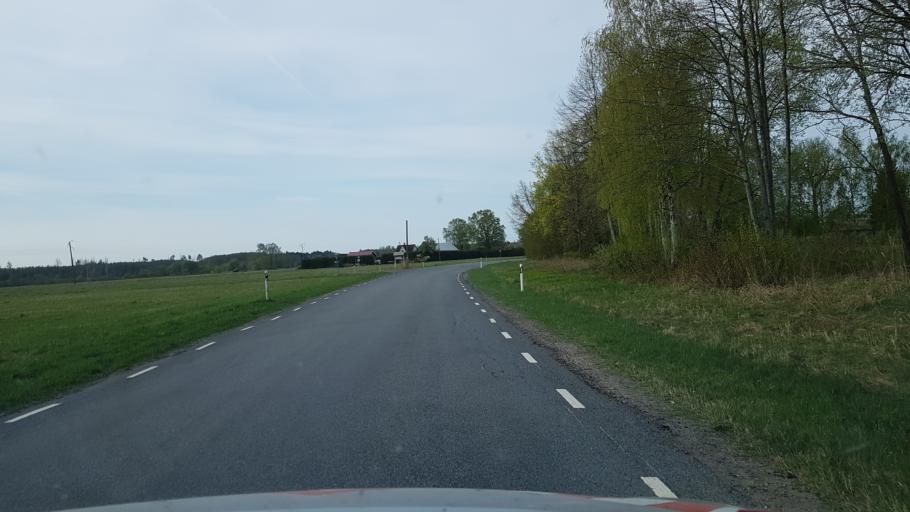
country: EE
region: Paernumaa
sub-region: Audru vald
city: Audru
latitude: 58.3645
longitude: 24.2634
